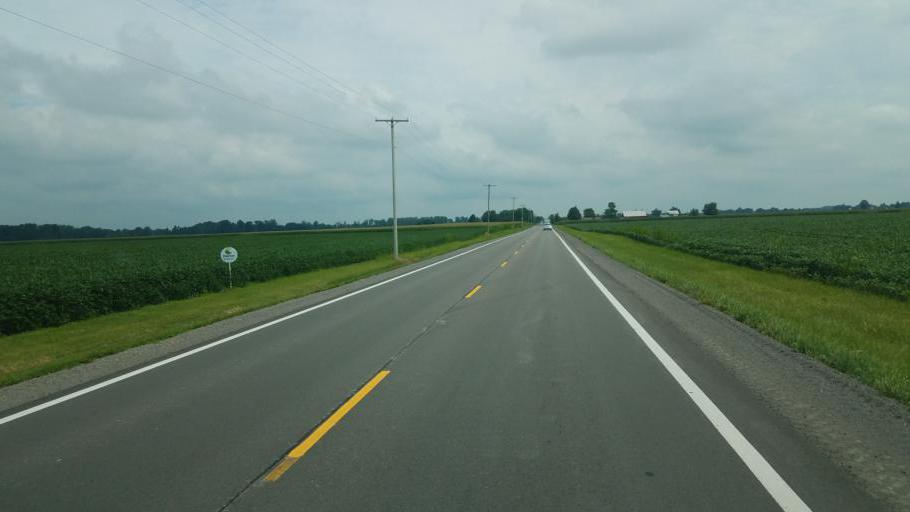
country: US
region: Ohio
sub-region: Marion County
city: Marion
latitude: 40.5903
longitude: -83.0376
